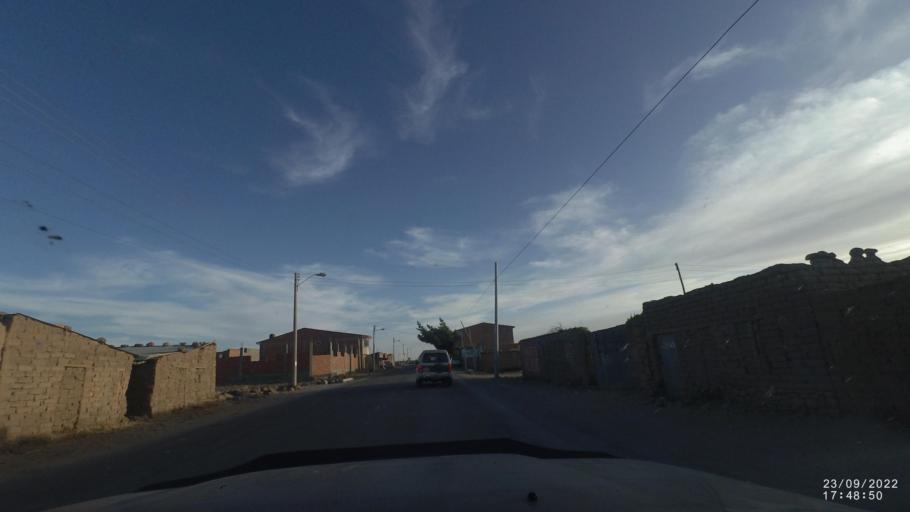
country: BO
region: Oruro
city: Challapata
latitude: -19.0181
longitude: -66.7774
